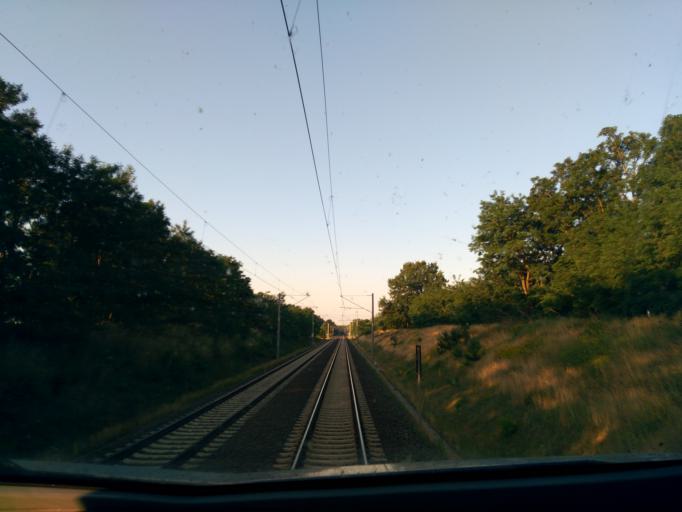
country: DE
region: Brandenburg
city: Halbe
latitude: 52.0641
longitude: 13.7248
